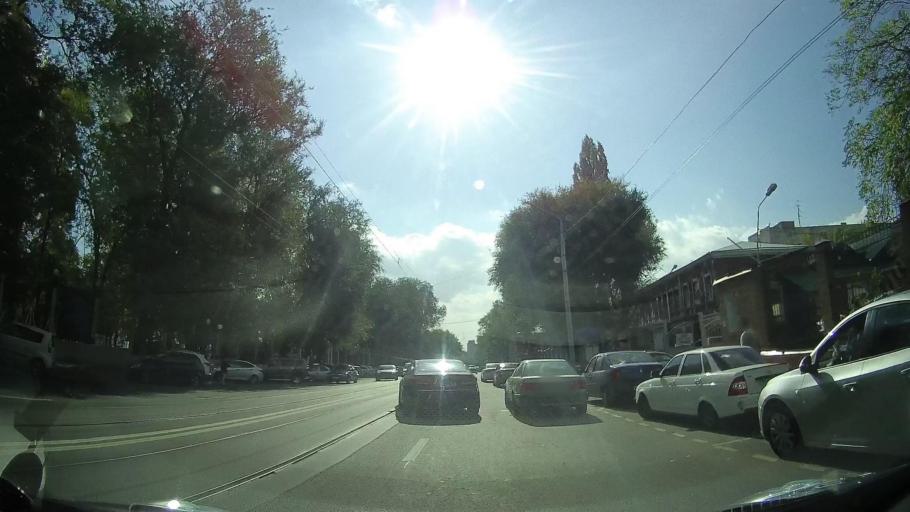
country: RU
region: Rostov
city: Rostov-na-Donu
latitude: 47.2298
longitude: 39.7416
